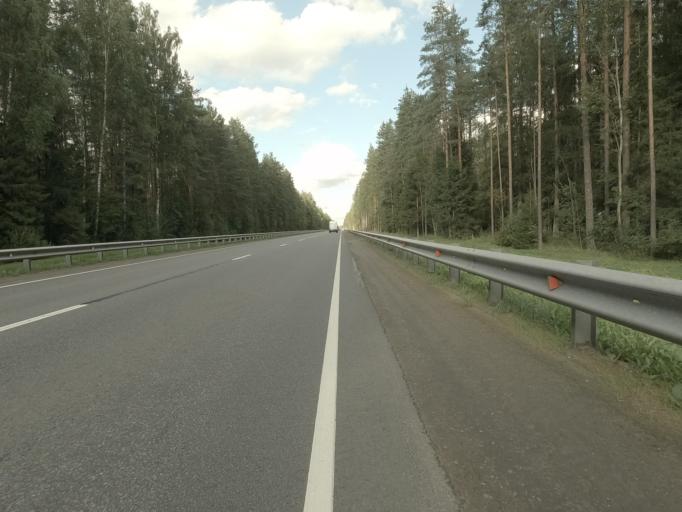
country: RU
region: Leningrad
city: Mga
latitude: 59.6983
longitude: 30.9932
